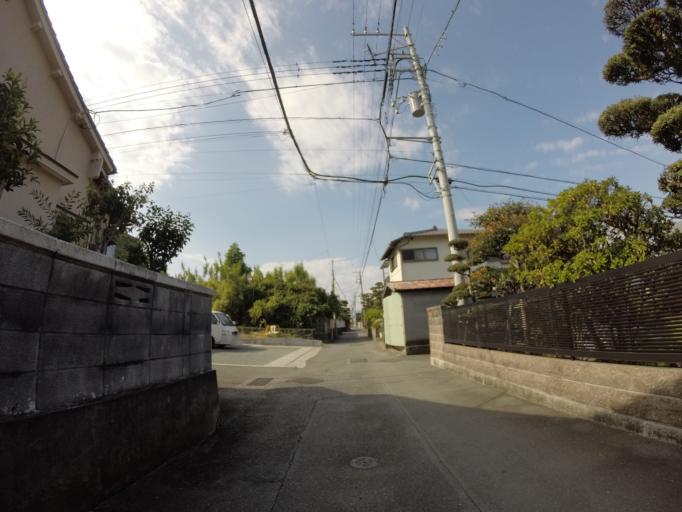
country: JP
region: Shizuoka
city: Fuji
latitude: 35.1373
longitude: 138.6894
